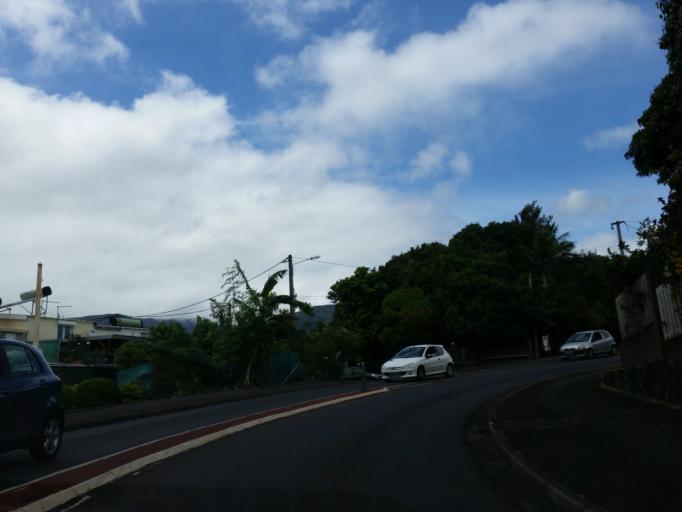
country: RE
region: Reunion
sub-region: Reunion
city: Saint-Denis
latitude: -20.9079
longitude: 55.4886
